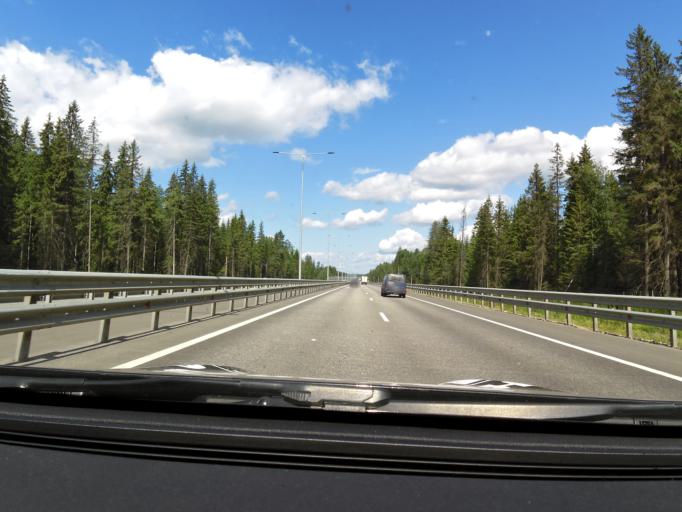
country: RU
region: Tverskaya
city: Vydropuzhsk
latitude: 57.3077
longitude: 34.7652
